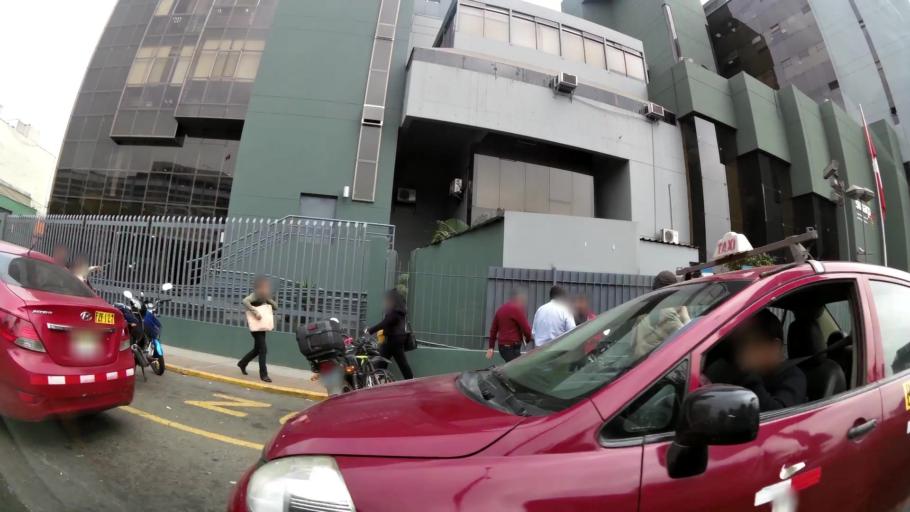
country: PE
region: Lima
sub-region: Lima
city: San Isidro
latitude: -12.0798
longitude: -77.0408
